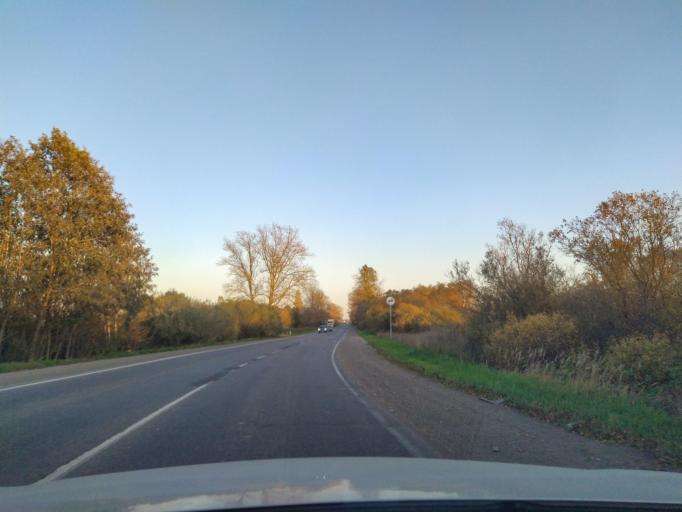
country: RU
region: Leningrad
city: Maloye Verevo
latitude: 59.6112
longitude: 30.2361
